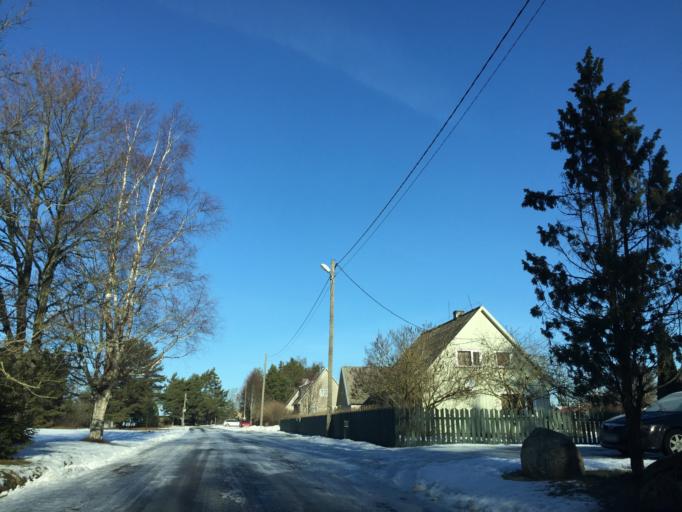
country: LV
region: Salacgrivas
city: Ainazi
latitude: 58.0807
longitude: 24.4904
